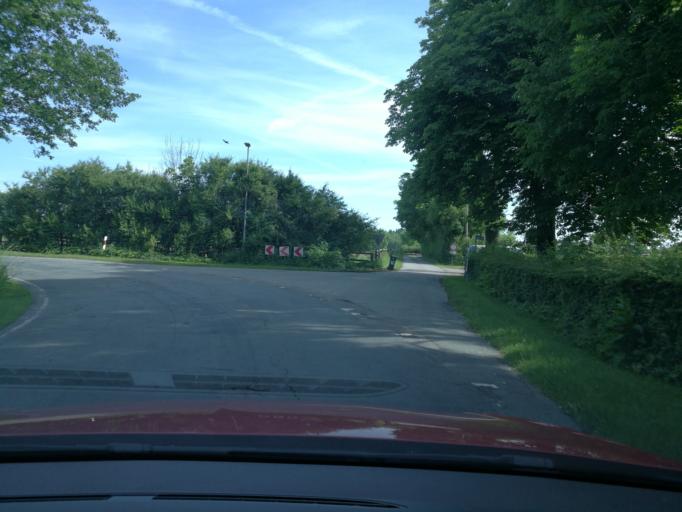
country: DE
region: Schleswig-Holstein
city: Lasbek
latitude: 53.7430
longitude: 10.3463
